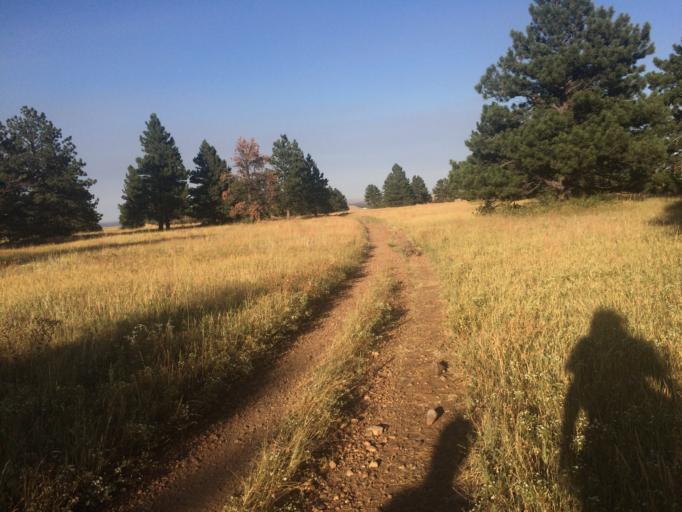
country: US
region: Colorado
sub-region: Boulder County
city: Superior
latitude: 39.9171
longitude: -105.2468
